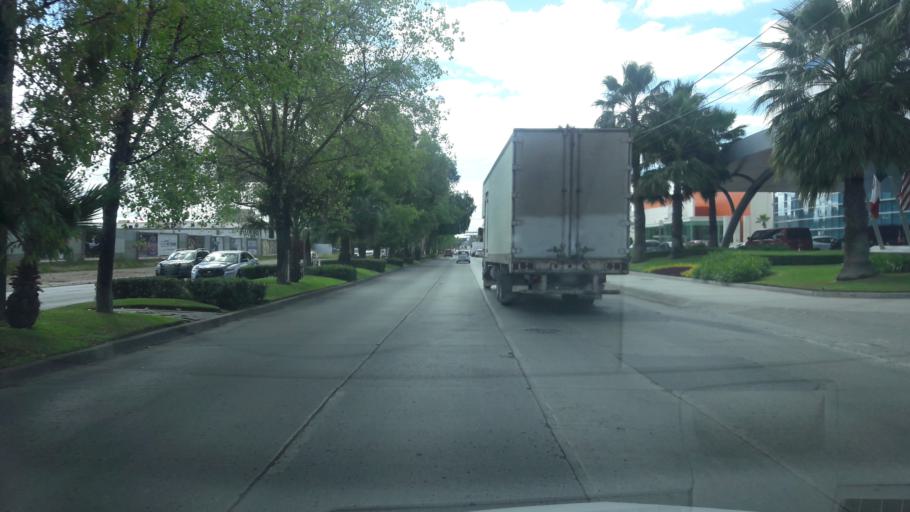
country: MX
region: Guanajuato
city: Leon
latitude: 21.1651
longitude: -101.6933
